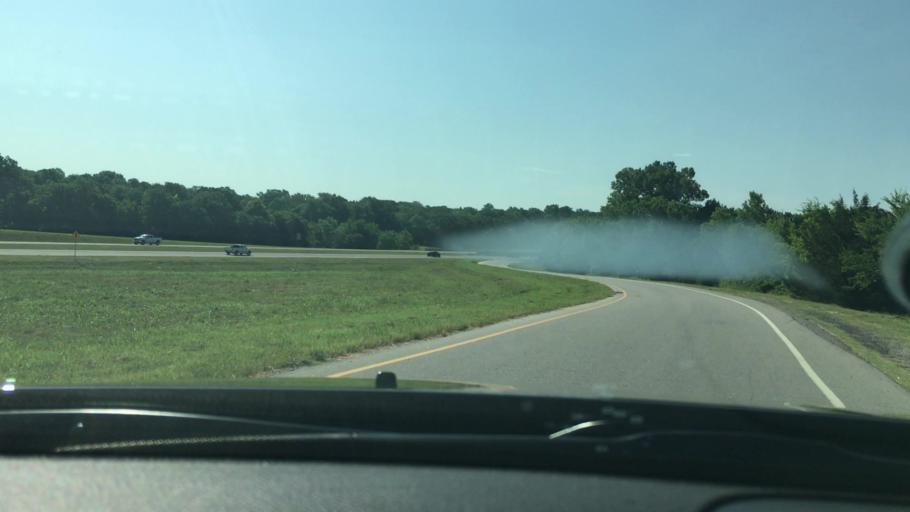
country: US
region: Oklahoma
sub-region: Pontotoc County
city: Ada
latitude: 34.7375
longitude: -96.6458
